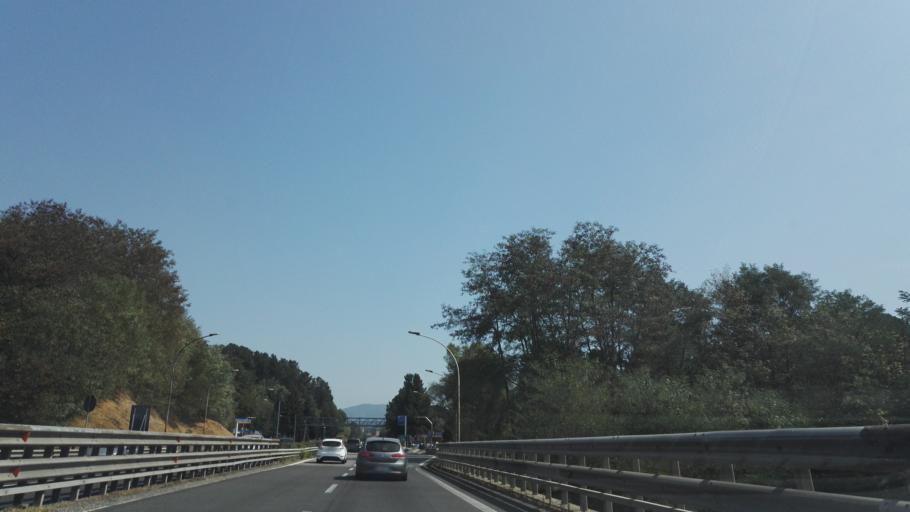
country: IT
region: Calabria
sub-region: Provincia di Cosenza
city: Rogliano
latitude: 39.1864
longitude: 16.3058
